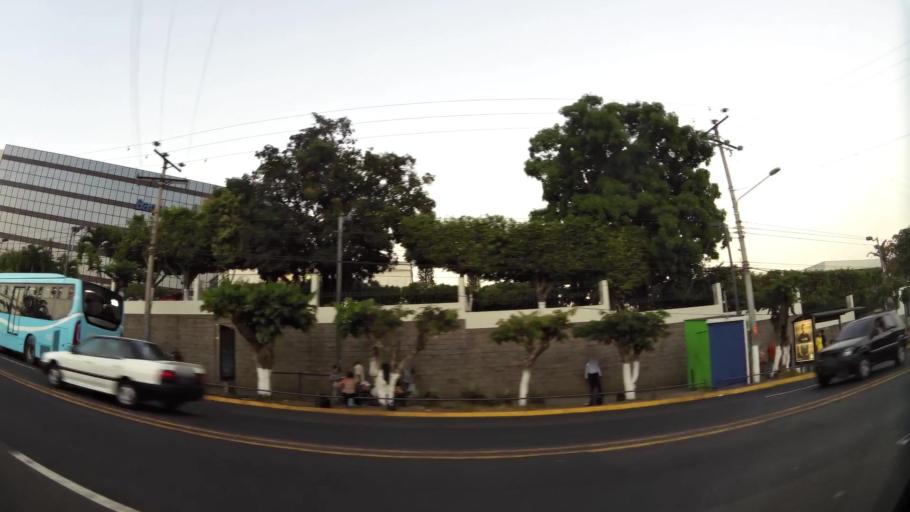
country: SV
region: San Salvador
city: Mejicanos
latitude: 13.7024
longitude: -89.2251
